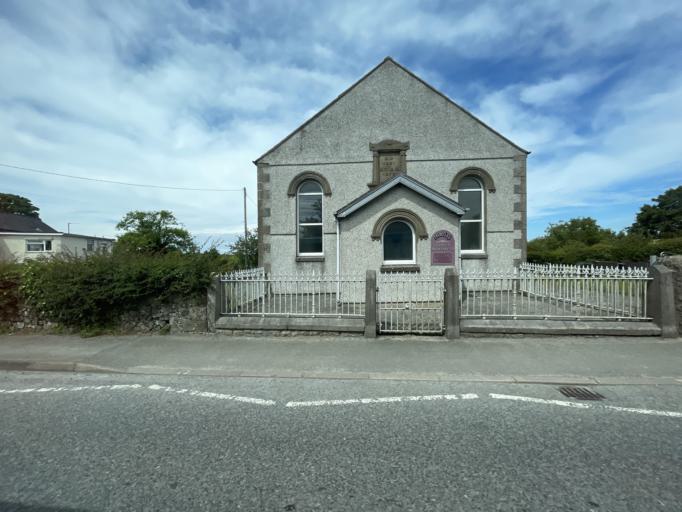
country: GB
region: Wales
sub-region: Anglesey
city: Gaerwen
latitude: 53.2227
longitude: -4.2737
